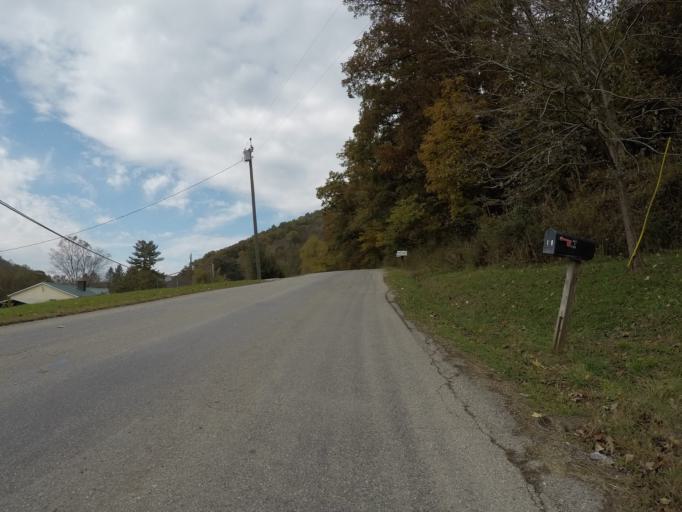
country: US
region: West Virginia
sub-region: Wayne County
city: Lavalette
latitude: 38.3355
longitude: -82.4412
